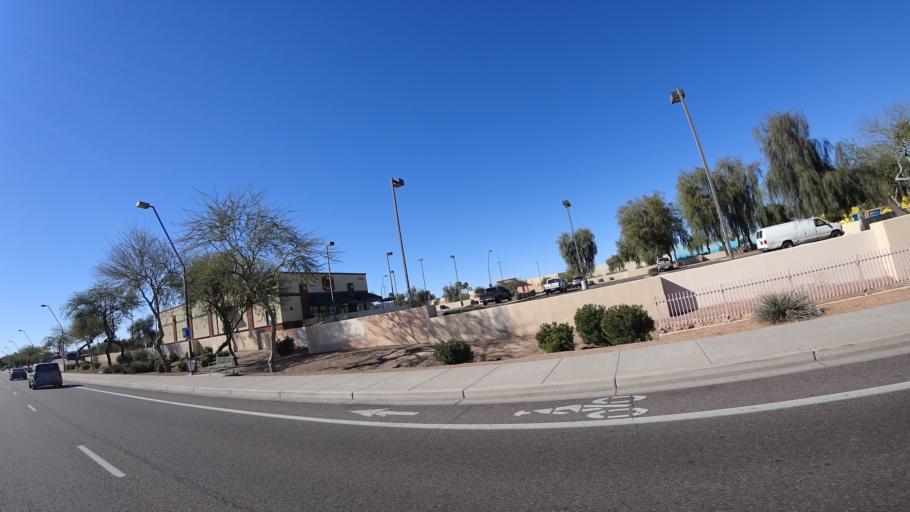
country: US
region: Arizona
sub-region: Maricopa County
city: Guadalupe
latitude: 33.3843
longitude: -111.9611
